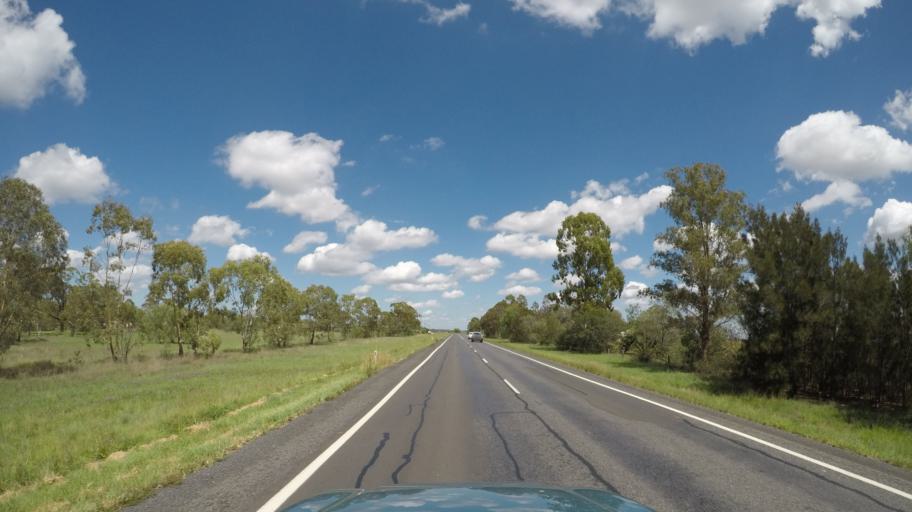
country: AU
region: Queensland
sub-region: Toowoomba
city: Oakey
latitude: -27.7551
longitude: 151.4517
